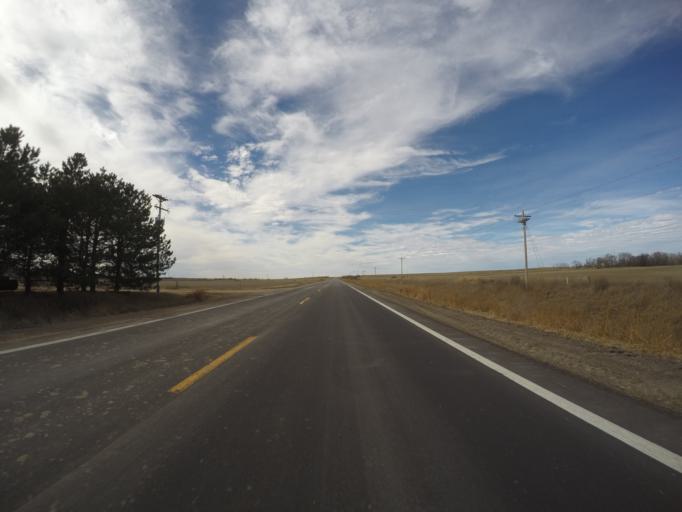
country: US
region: Nebraska
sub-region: Franklin County
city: Franklin
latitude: 40.0962
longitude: -98.8536
